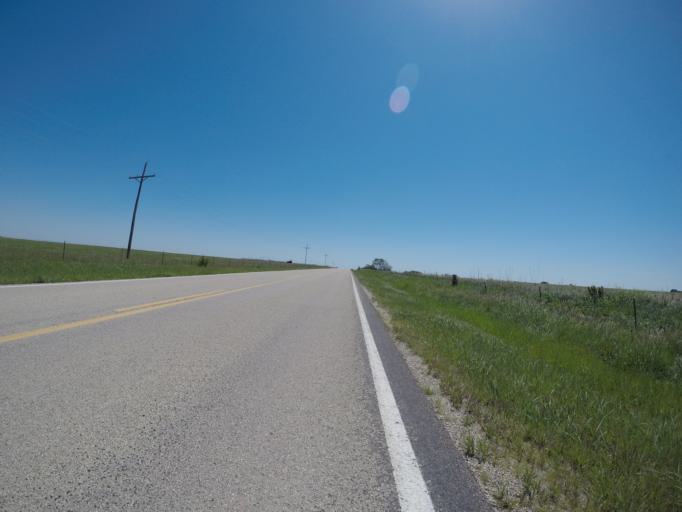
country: US
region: Kansas
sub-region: Shawnee County
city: Auburn
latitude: 38.8847
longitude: -95.9962
